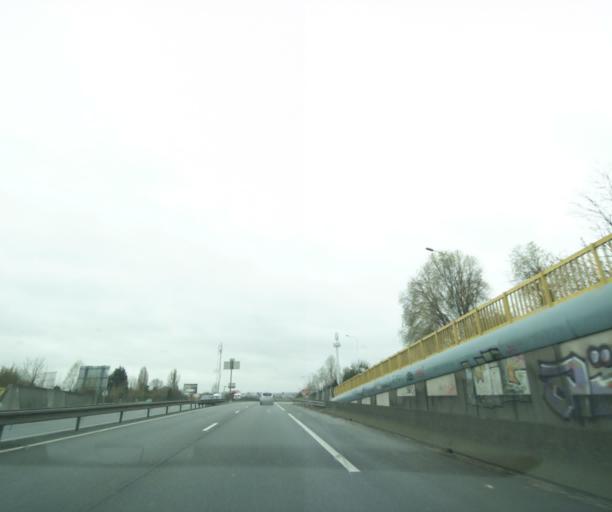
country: FR
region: Ile-de-France
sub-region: Departement de l'Essonne
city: Arpajon
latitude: 48.5975
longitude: 2.2445
